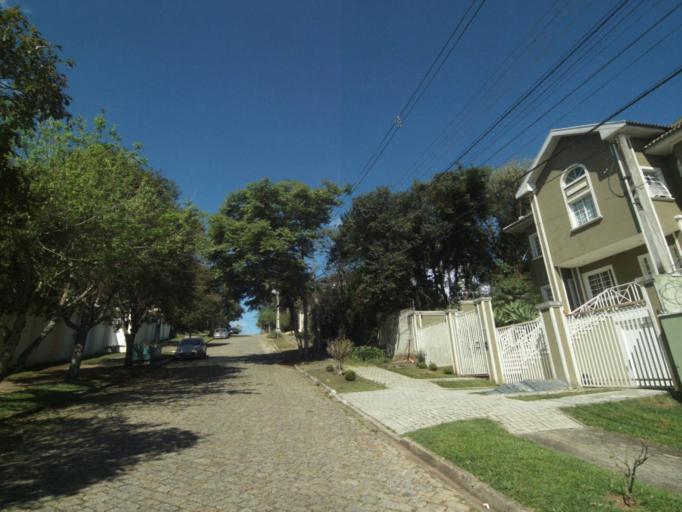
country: BR
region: Parana
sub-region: Curitiba
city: Curitiba
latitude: -25.3998
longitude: -49.2698
